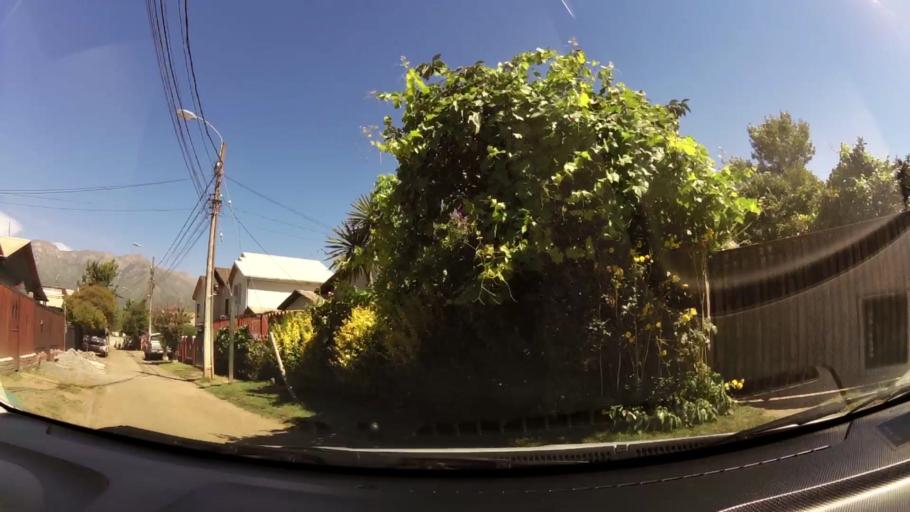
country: CL
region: O'Higgins
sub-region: Provincia de Cachapoal
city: Graneros
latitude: -33.9725
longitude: -70.7074
